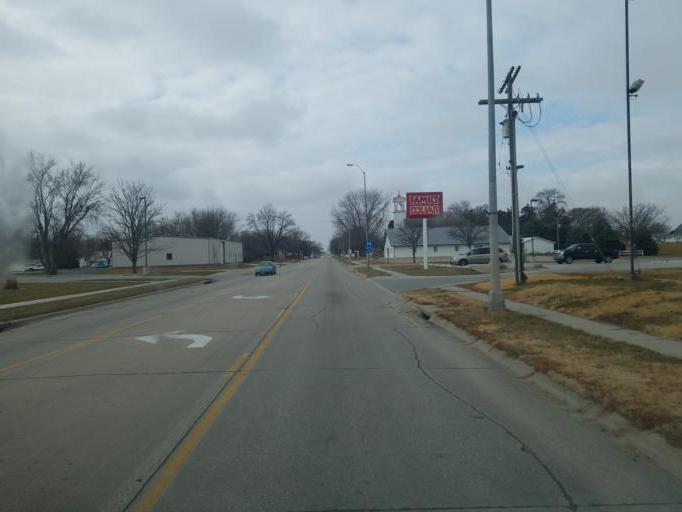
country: US
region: Nebraska
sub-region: Pierce County
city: Plainview
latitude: 42.3509
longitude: -97.7841
